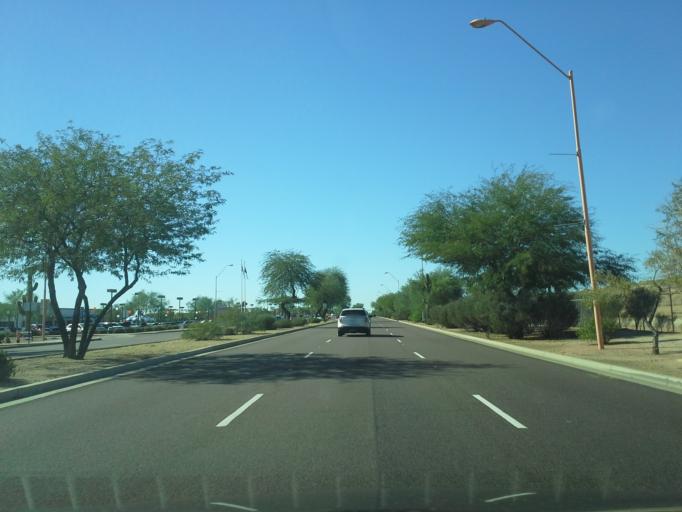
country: US
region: Arizona
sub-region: Maricopa County
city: Paradise Valley
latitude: 33.6348
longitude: -111.9089
